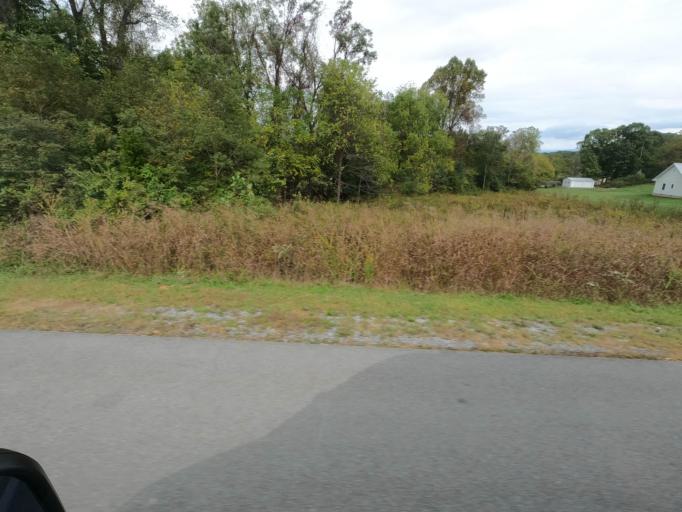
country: US
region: Tennessee
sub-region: Carter County
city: Central
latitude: 36.3232
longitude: -82.2562
